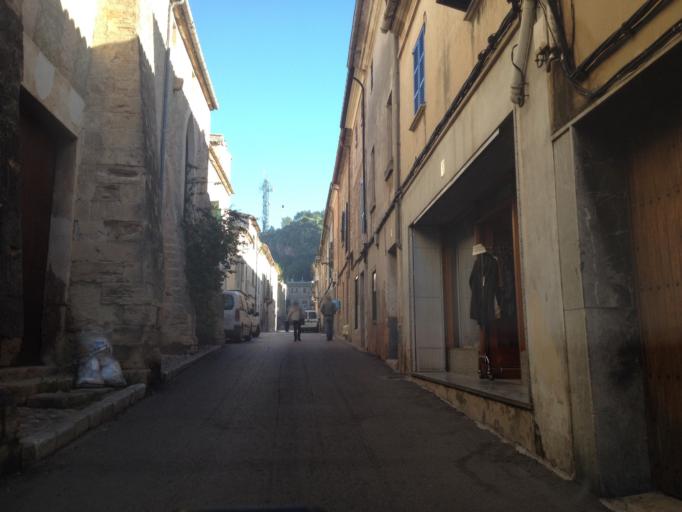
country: ES
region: Balearic Islands
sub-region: Illes Balears
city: Pollenca
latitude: 39.8793
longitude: 3.0182
